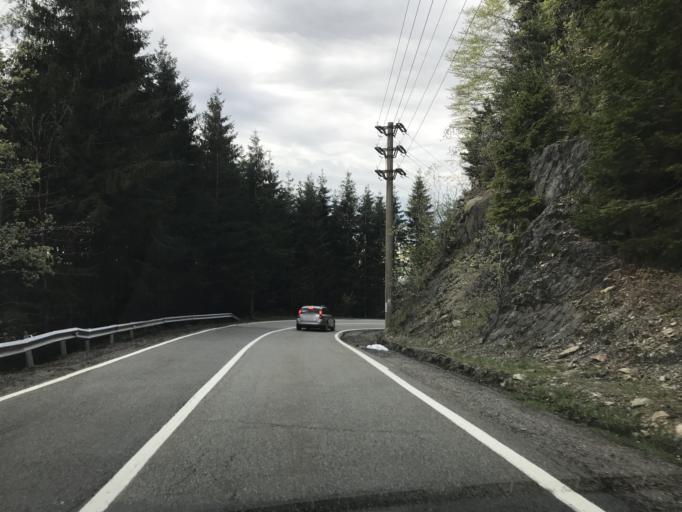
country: RO
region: Sibiu
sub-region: Comuna Cartisoara
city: Cartisoara
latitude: 45.6498
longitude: 24.6050
